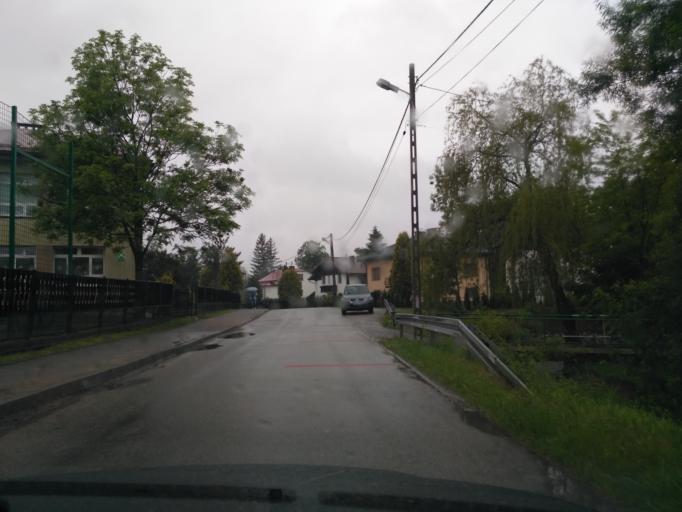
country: PL
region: Lesser Poland Voivodeship
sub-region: Powiat gorlicki
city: Gorlice
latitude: 49.6674
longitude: 21.1415
